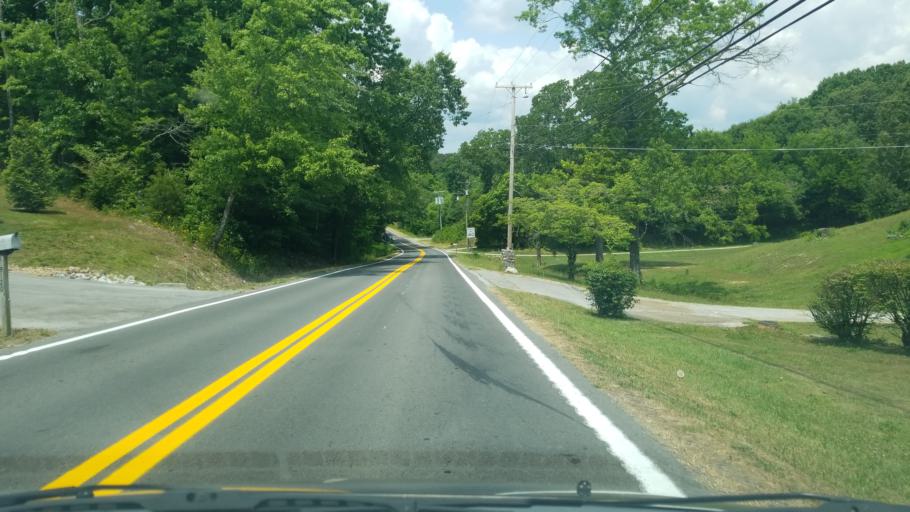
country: US
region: Tennessee
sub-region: Hamilton County
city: Lakesite
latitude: 35.2045
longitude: -85.1403
